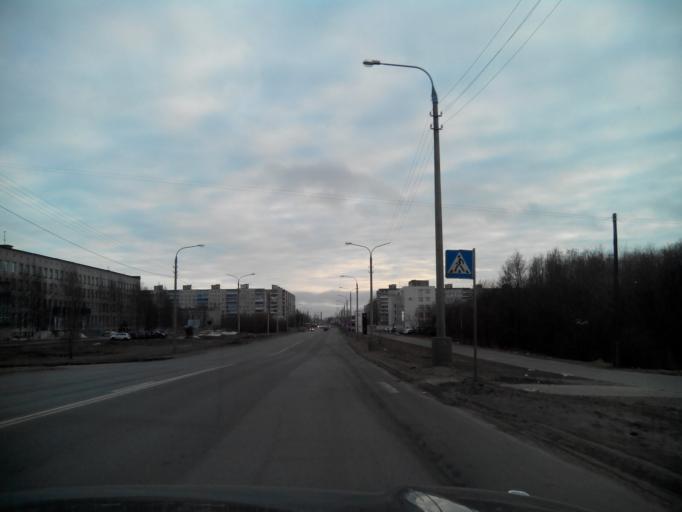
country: RU
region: Arkhangelskaya
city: Arkhangel'sk
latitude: 64.5179
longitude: 40.6771
